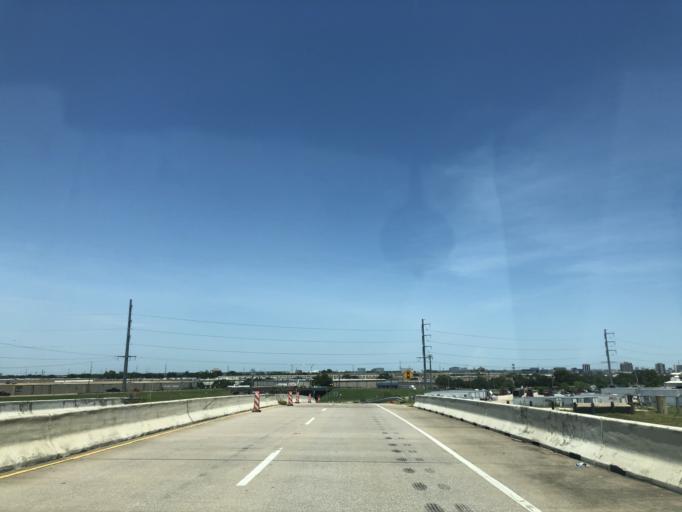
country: US
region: Texas
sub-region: Dallas County
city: Irving
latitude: 32.8065
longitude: -96.9025
